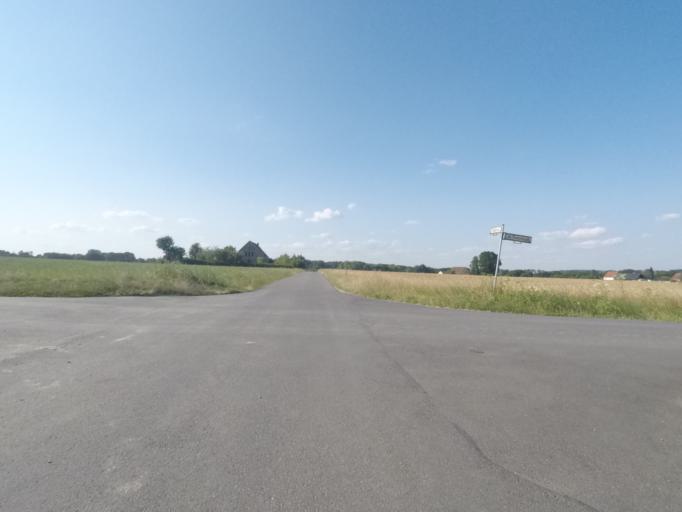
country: DE
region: North Rhine-Westphalia
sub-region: Regierungsbezirk Detmold
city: Hiddenhausen
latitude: 52.1036
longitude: 8.6108
